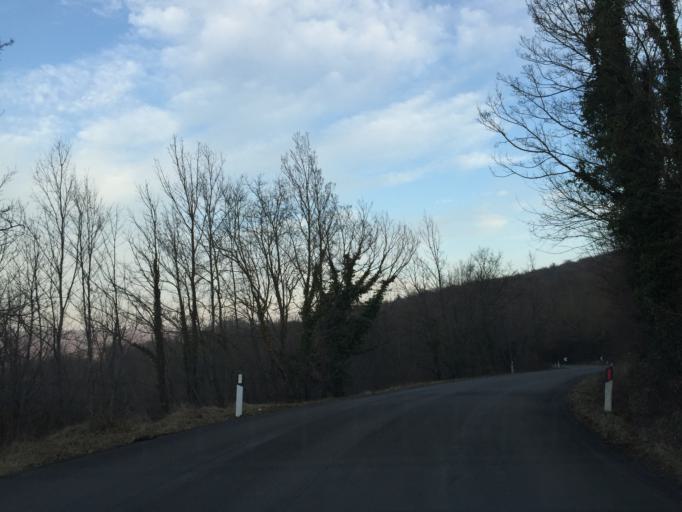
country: IT
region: Molise
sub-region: Provincia di Campobasso
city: Guardiaregia
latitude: 41.4479
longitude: 14.5525
